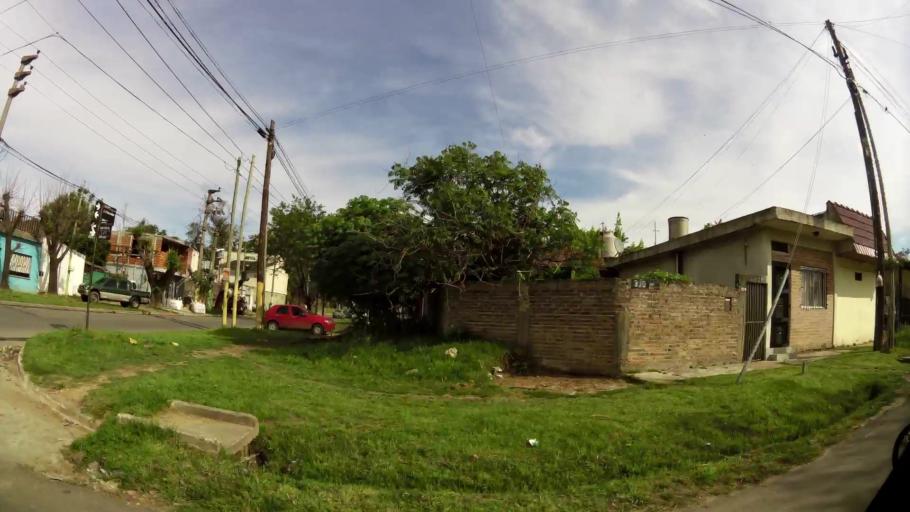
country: AR
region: Buenos Aires
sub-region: Partido de Quilmes
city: Quilmes
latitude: -34.7492
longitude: -58.2753
